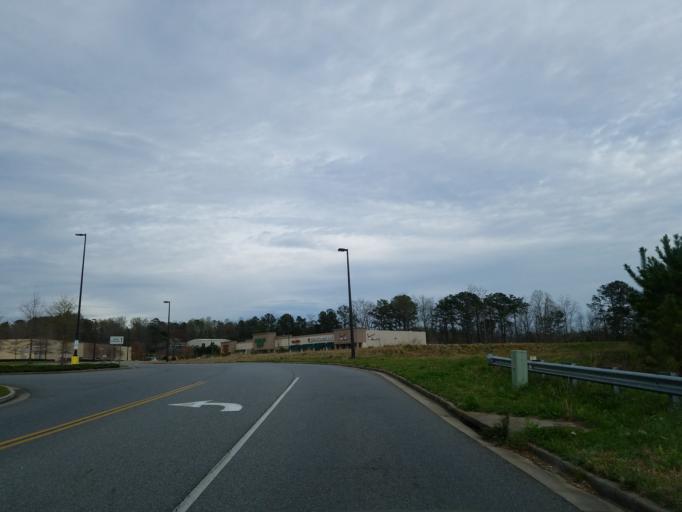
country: US
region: Georgia
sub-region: Pickens County
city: Jasper
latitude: 34.4737
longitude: -84.4613
